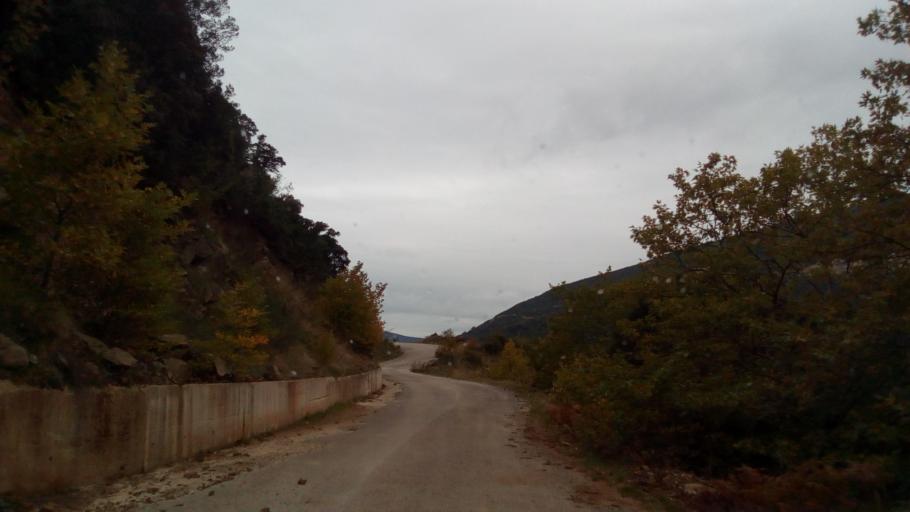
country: GR
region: West Greece
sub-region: Nomos Aitolias kai Akarnanias
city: Thermo
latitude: 38.6098
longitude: 21.8427
